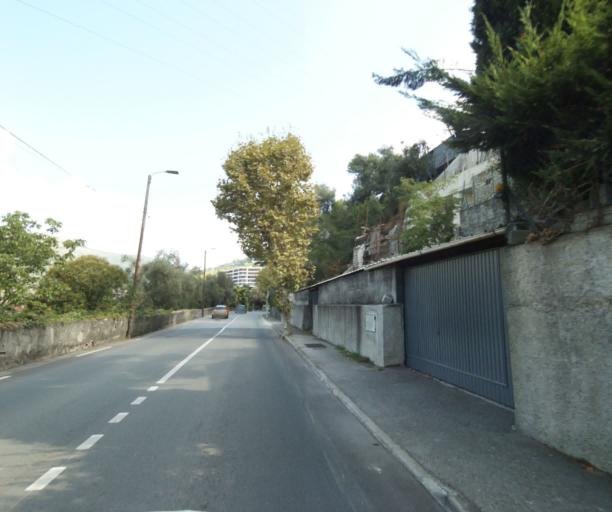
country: FR
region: Provence-Alpes-Cote d'Azur
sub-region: Departement des Alpes-Maritimes
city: La Trinite
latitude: 43.7466
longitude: 7.3199
